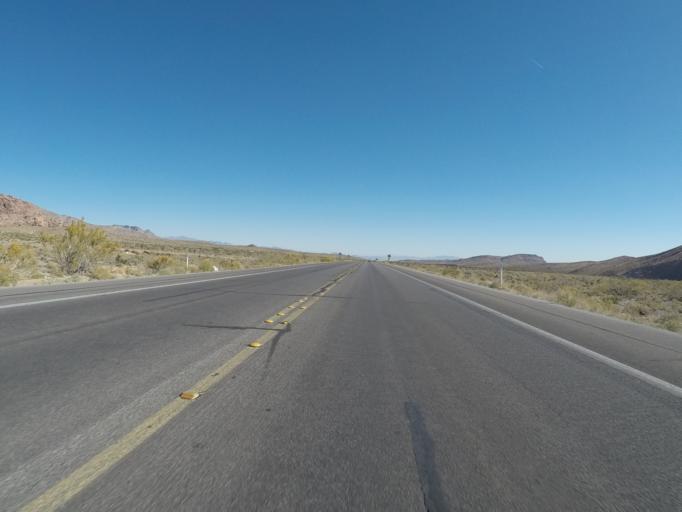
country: US
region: Nevada
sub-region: Clark County
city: Summerlin South
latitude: 36.1287
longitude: -115.4277
